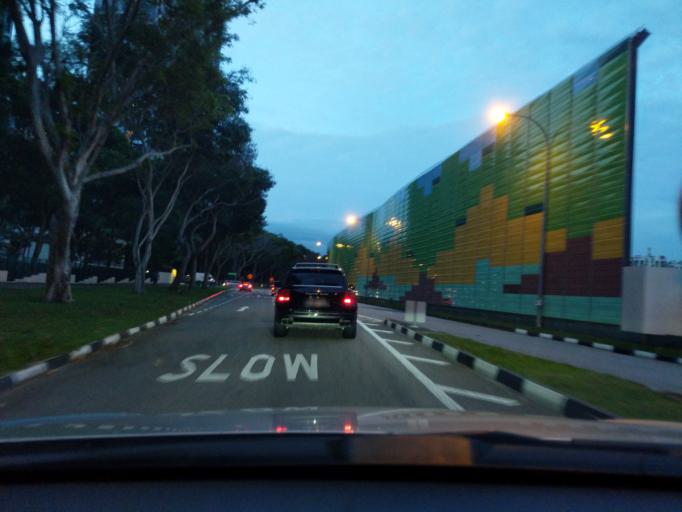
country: SG
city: Singapore
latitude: 1.3116
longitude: 103.9408
